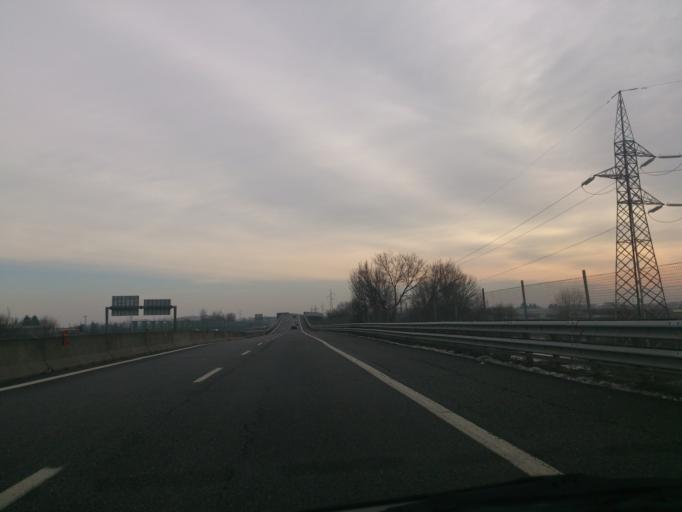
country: IT
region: Lombardy
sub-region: Citta metropolitana di Milano
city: San Donato Milanese
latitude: 45.4112
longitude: 9.2618
